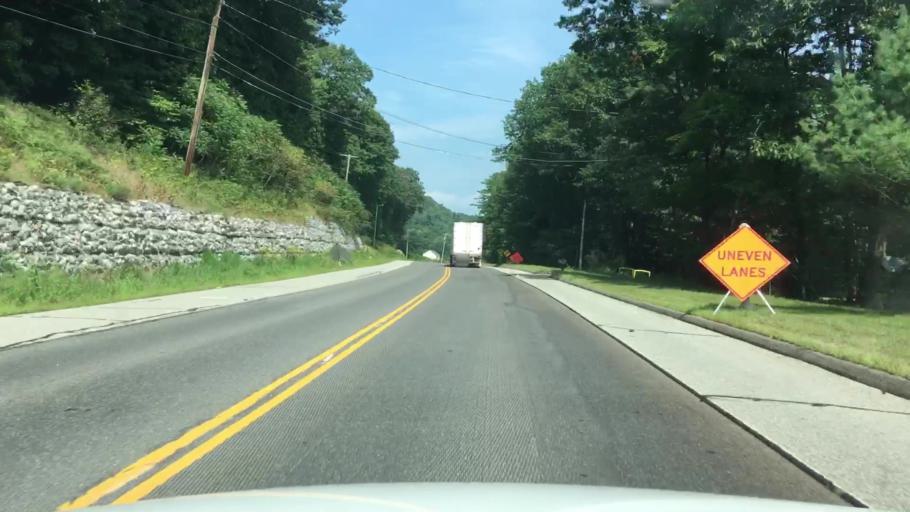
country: US
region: Maine
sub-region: Androscoggin County
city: Turner
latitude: 44.3079
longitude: -70.2660
